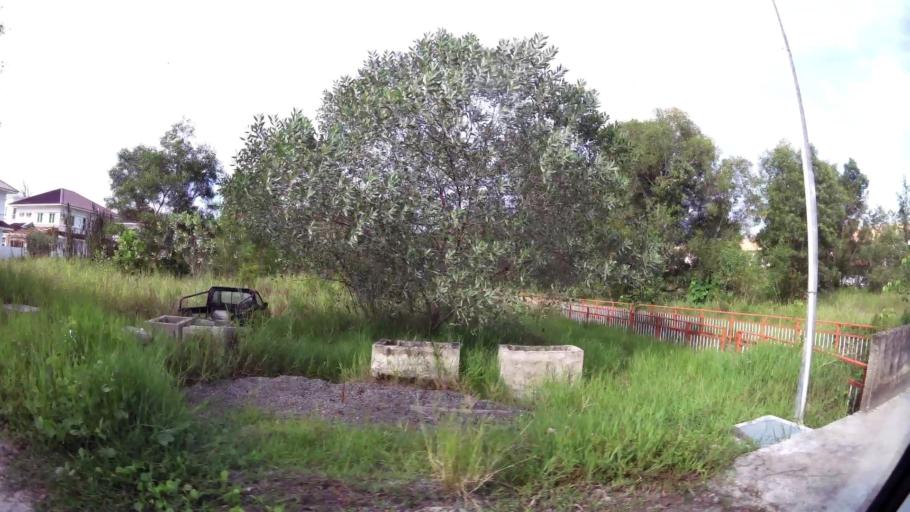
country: BN
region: Brunei and Muara
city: Bandar Seri Begawan
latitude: 4.9037
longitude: 114.8910
